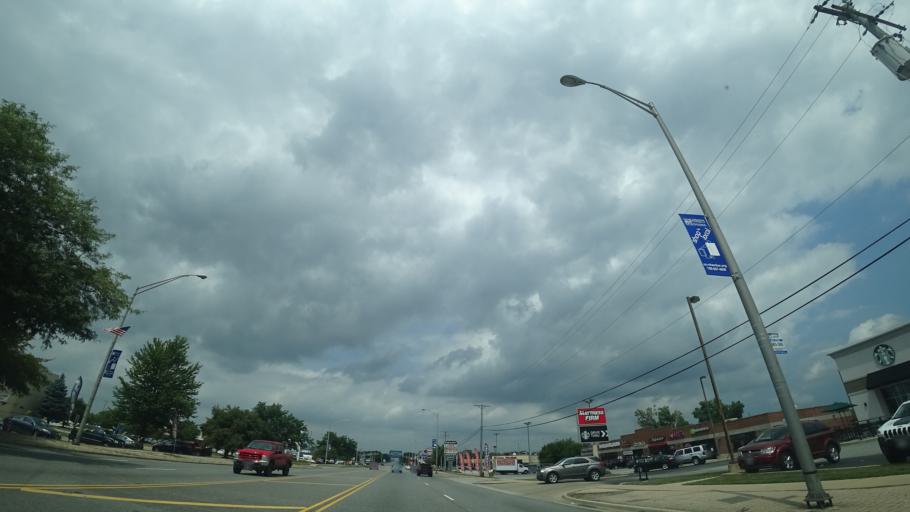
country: US
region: Illinois
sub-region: Cook County
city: Crestwood
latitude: 41.6511
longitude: -87.7382
